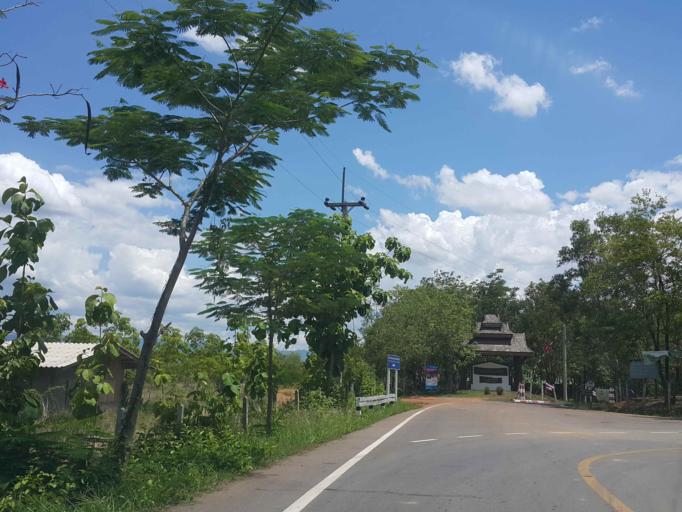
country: TH
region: Phrae
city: Phrae
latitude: 18.1850
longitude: 100.2116
